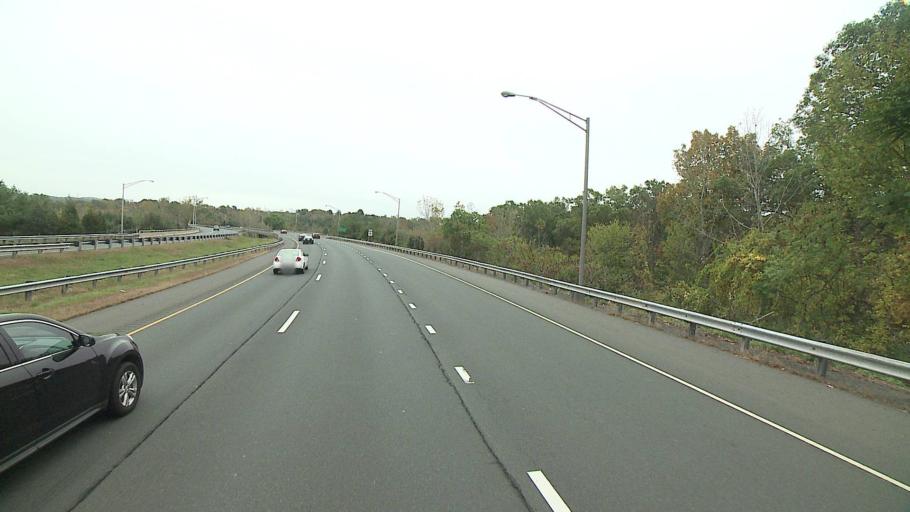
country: US
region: Connecticut
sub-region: Hartford County
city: Kensington
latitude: 41.6214
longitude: -72.7349
